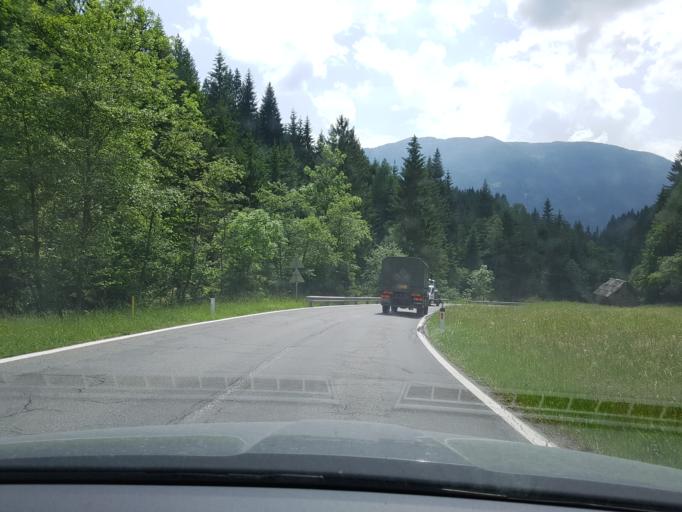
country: AT
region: Carinthia
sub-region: Politischer Bezirk Villach Land
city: Feld am See
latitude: 46.8033
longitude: 13.7568
